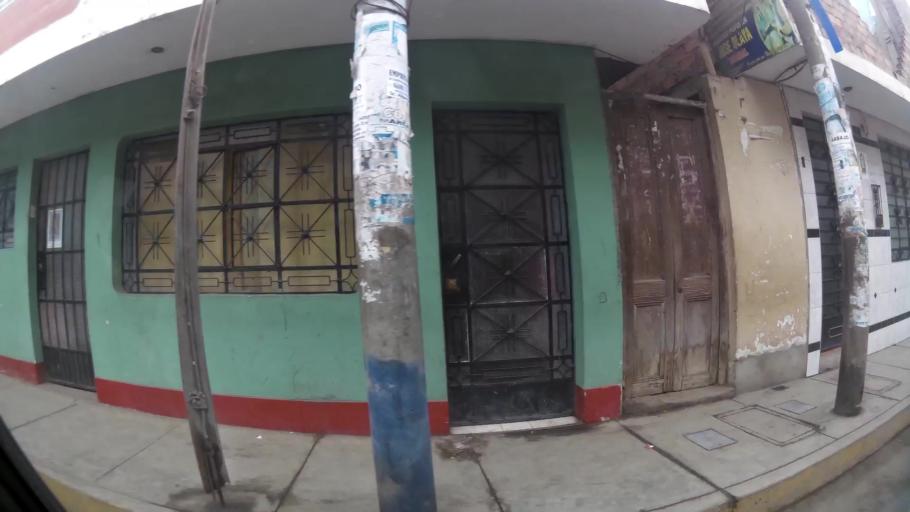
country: PE
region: Lima
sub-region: Provincia de Huaral
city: Huaral
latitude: -11.4977
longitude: -77.2096
